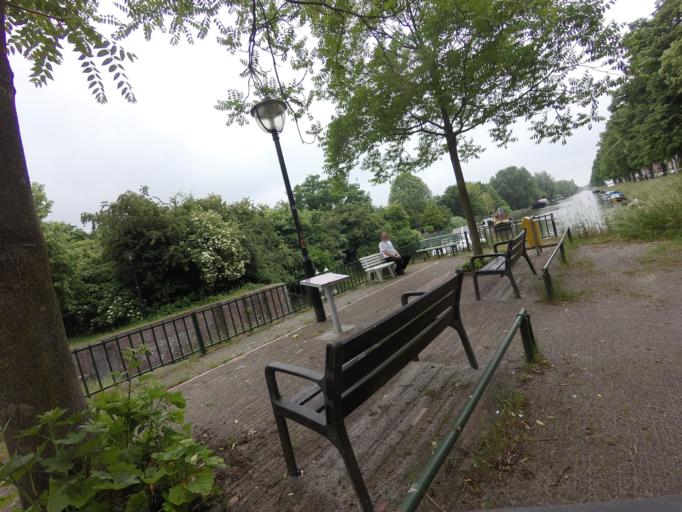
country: NL
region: Utrecht
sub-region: Gemeente Utrecht
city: Utrecht
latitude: 52.0721
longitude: 5.1185
